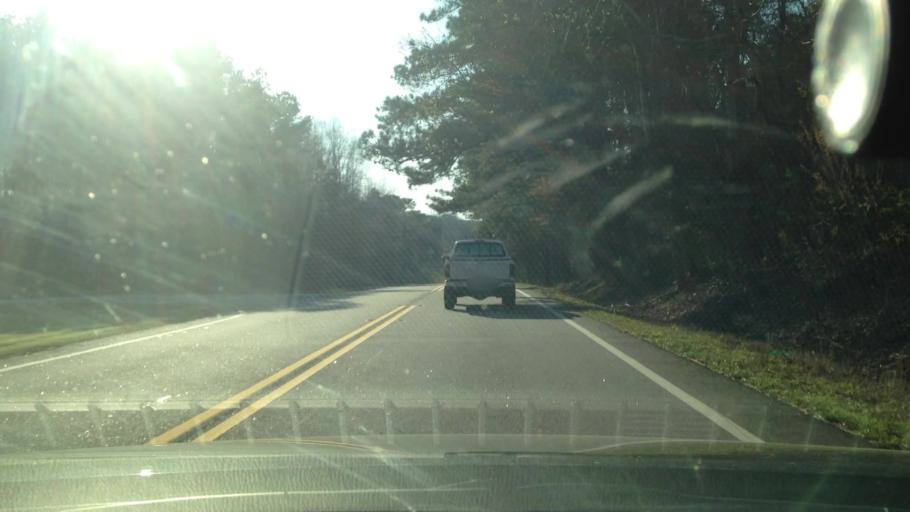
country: US
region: Georgia
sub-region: Fayette County
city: Peachtree City
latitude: 33.3395
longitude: -84.6563
